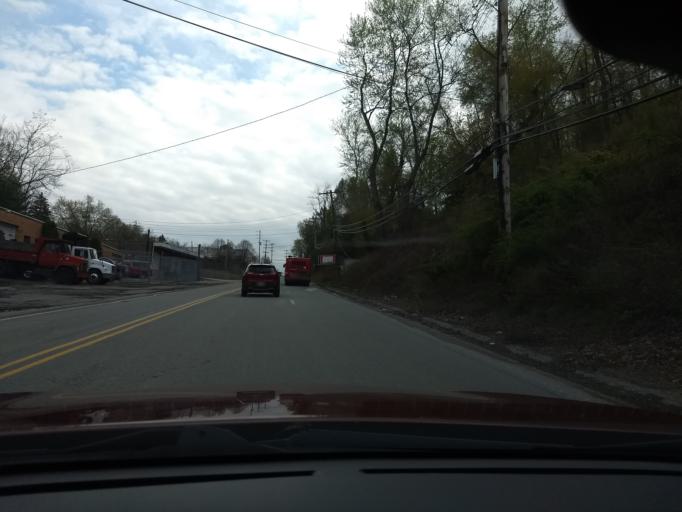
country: US
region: Pennsylvania
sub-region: Allegheny County
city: Wilkinsburg
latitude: 40.4652
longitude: -79.8655
